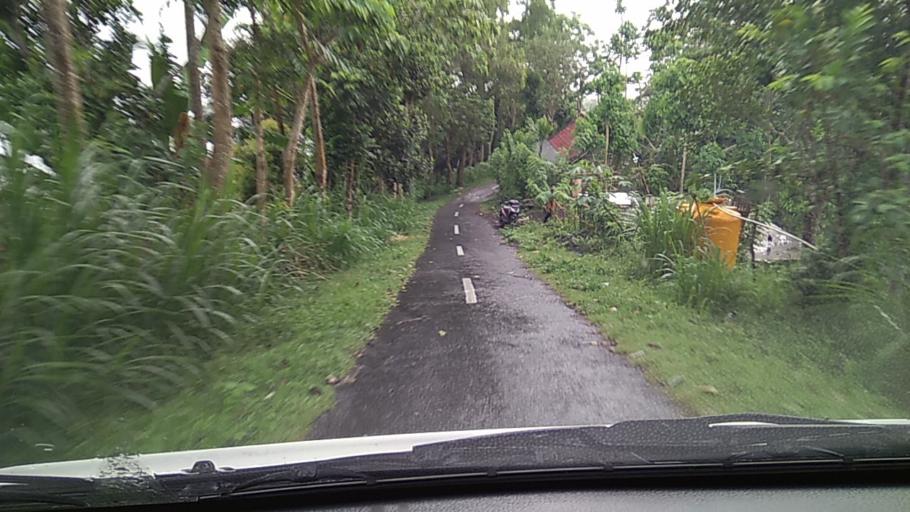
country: ID
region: Bali
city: Tiyingtali Kelod
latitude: -8.3976
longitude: 115.6335
